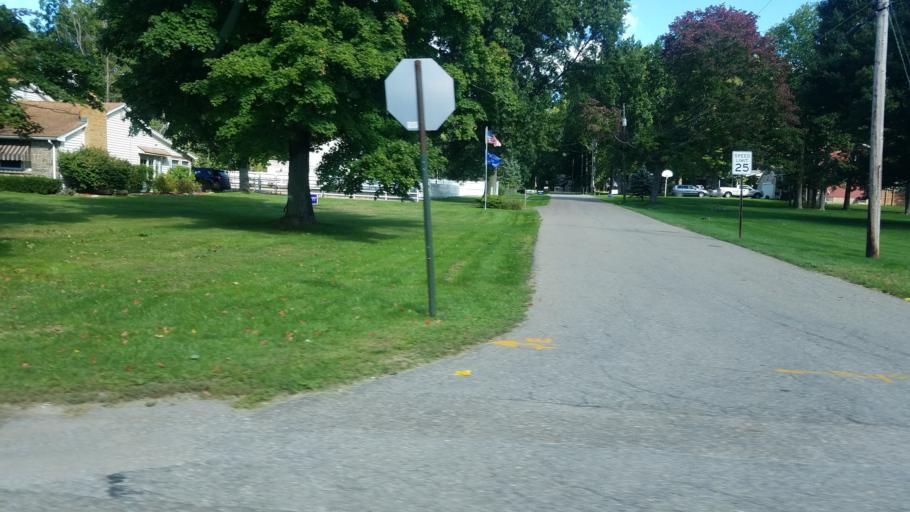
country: US
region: Ohio
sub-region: Mahoning County
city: Canfield
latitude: 41.0458
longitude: -80.7606
